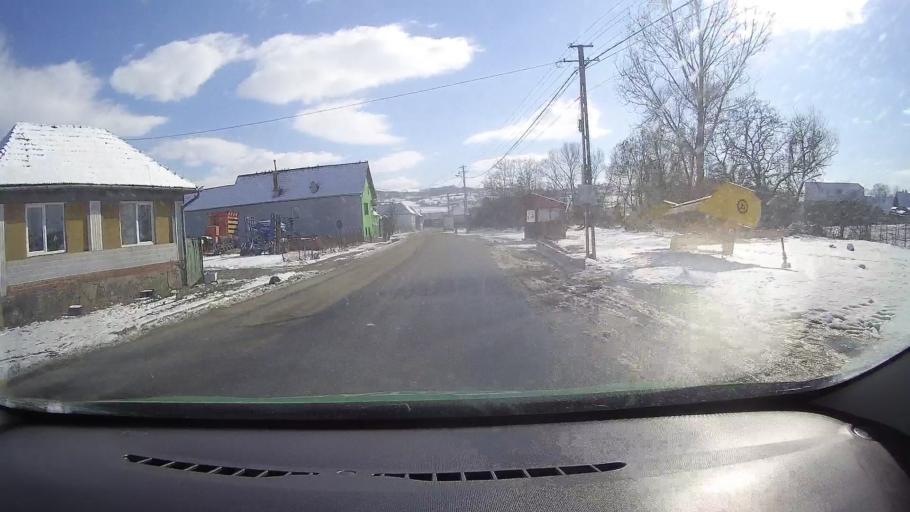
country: RO
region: Sibiu
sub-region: Comuna Barghis
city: Barghis
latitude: 45.9887
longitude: 24.4849
